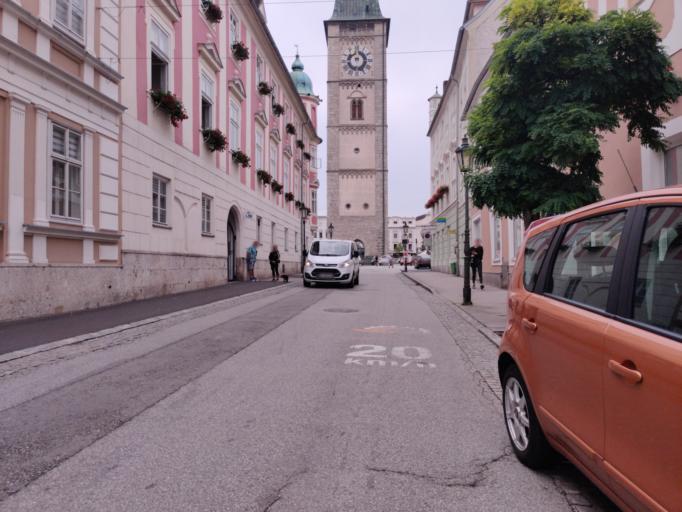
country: AT
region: Upper Austria
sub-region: Politischer Bezirk Linz-Land
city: Enns
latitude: 48.2149
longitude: 14.4797
